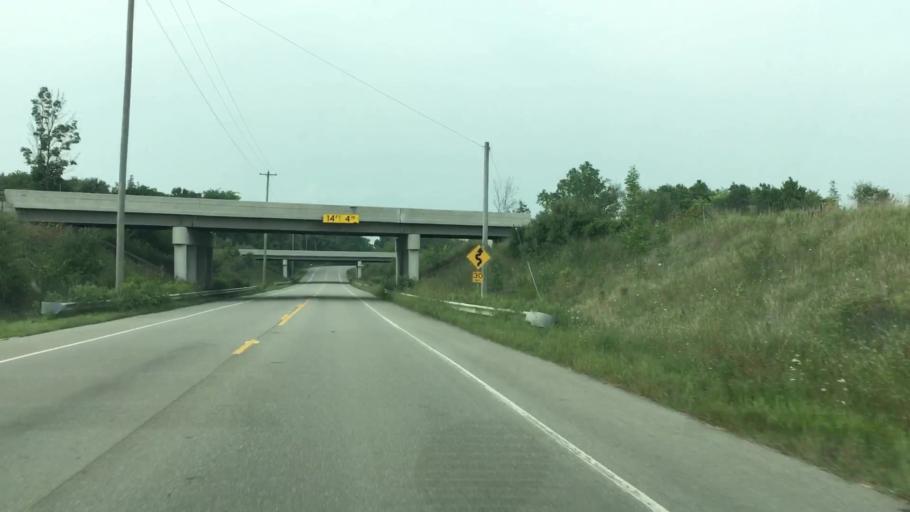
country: US
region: Michigan
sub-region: Ottawa County
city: Hudsonville
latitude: 42.8347
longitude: -85.9006
